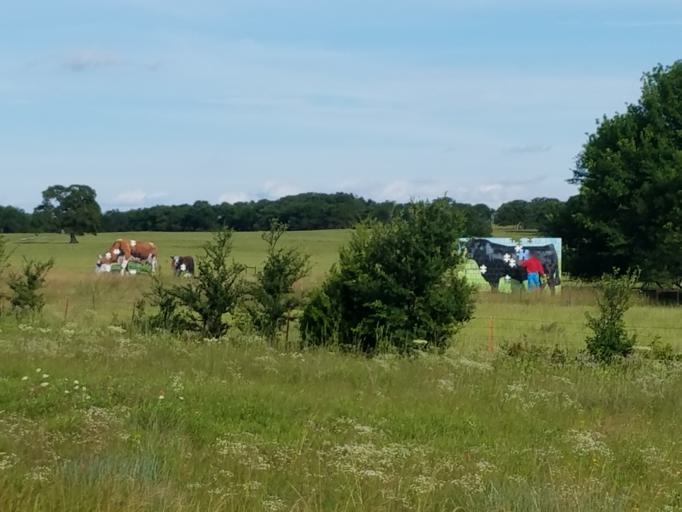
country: US
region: Oklahoma
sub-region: Coal County
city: Coalgate
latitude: 34.6000
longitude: -96.3311
